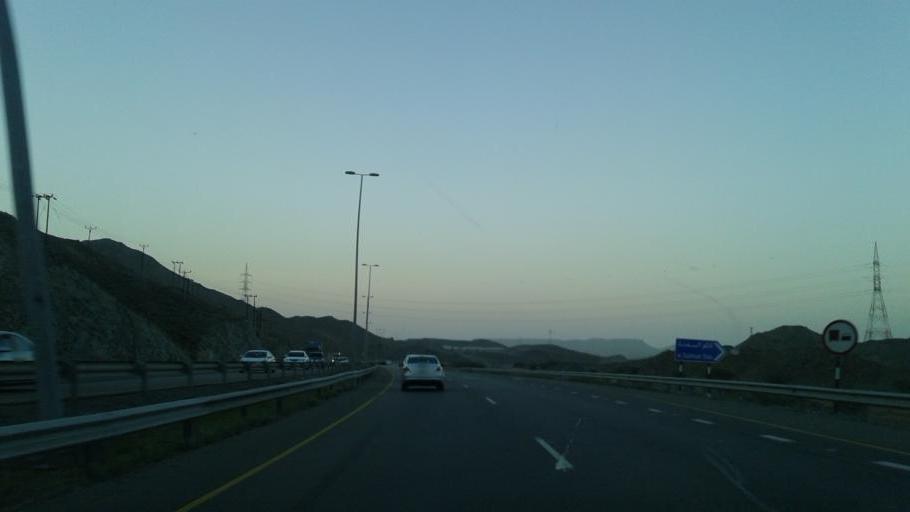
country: OM
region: Muhafazat ad Dakhiliyah
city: Bidbid
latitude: 23.4721
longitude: 58.1963
